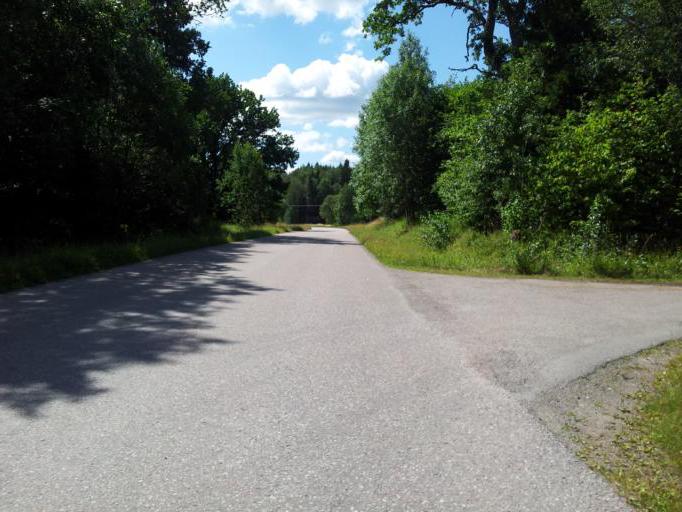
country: SE
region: Uppsala
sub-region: Knivsta Kommun
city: Knivsta
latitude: 59.8486
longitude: 17.9149
